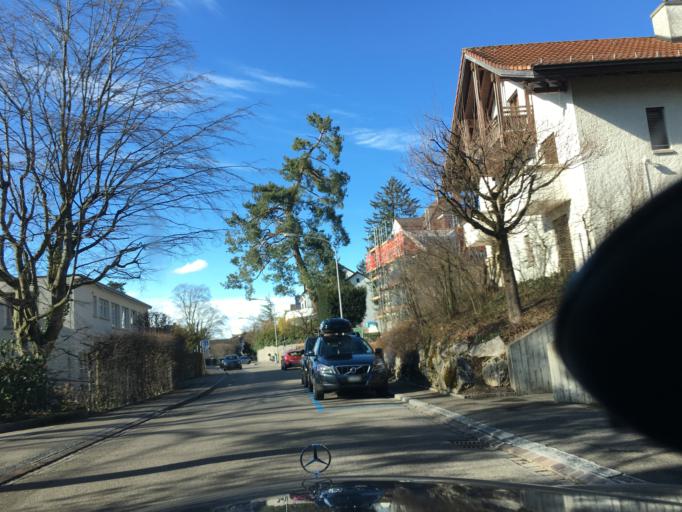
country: CH
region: Zurich
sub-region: Bezirk Zuerich
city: Zuerich (Kreis 8) / Weinegg
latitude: 47.3562
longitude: 8.5795
